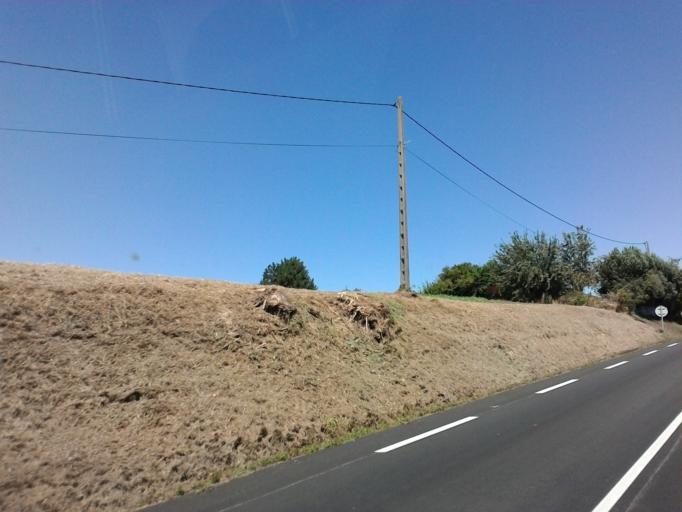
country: FR
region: Rhone-Alpes
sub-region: Departement de l'Ain
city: Saint-Etienne-du-Bois
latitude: 46.3337
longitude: 5.3163
